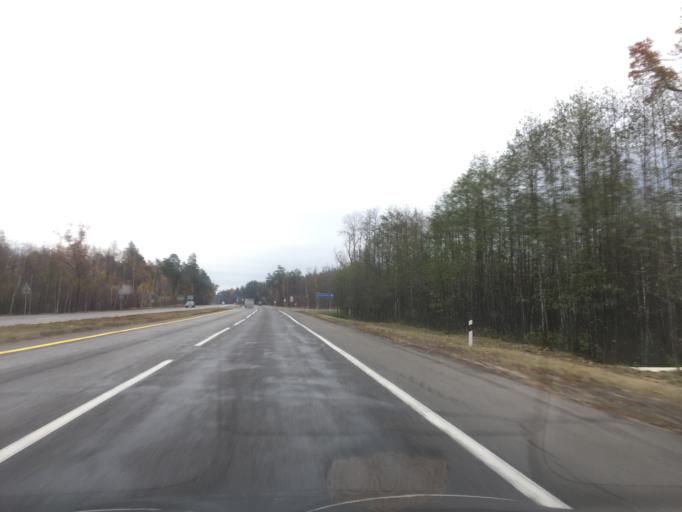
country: BY
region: Gomel
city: Kastsyukowka
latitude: 52.3570
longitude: 30.7012
